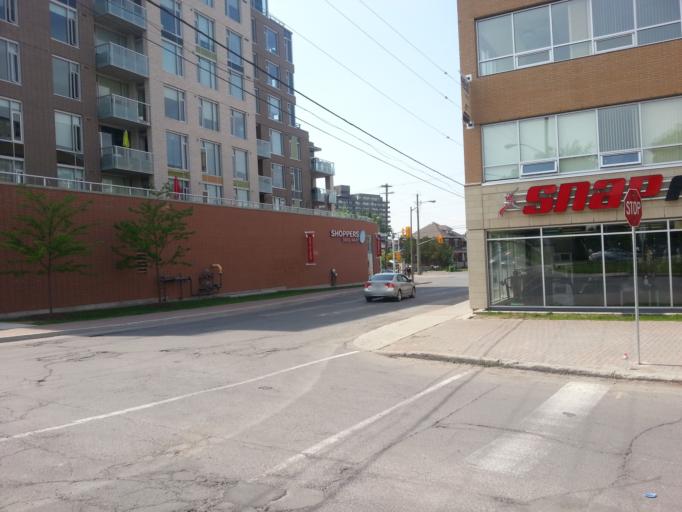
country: CA
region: Ontario
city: Ottawa
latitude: 45.3902
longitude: -75.7562
